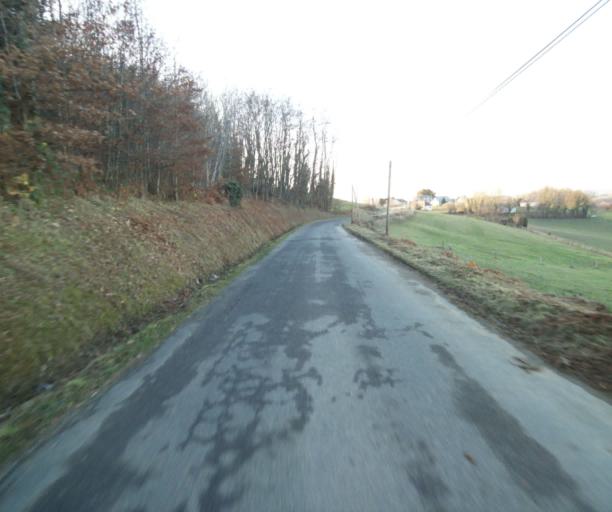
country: FR
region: Limousin
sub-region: Departement de la Correze
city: Laguenne
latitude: 45.2349
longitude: 1.8207
